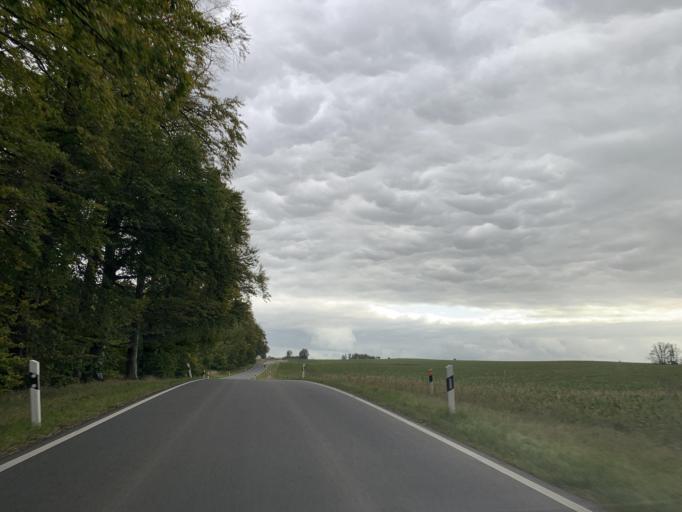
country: DE
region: Mecklenburg-Vorpommern
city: Burg Stargard
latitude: 53.4741
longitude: 13.2919
